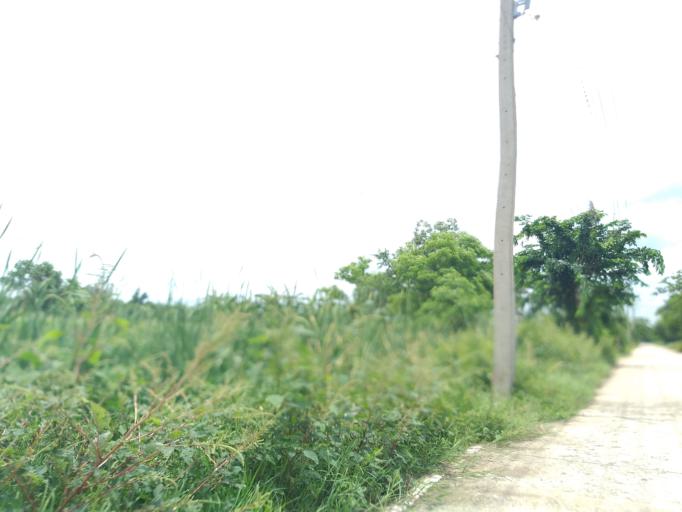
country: TH
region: Pathum Thani
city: Ban Lam Luk Ka
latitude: 13.9901
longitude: 100.8605
